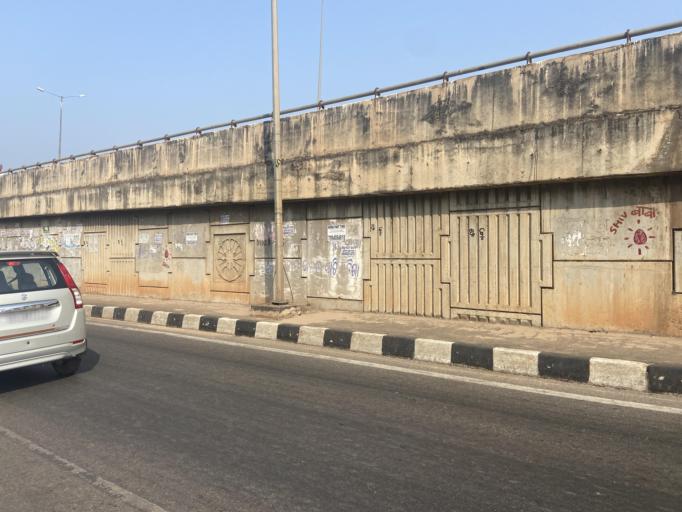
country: IN
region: Odisha
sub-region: Khordha
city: Bhubaneshwar
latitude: 20.2958
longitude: 85.8451
